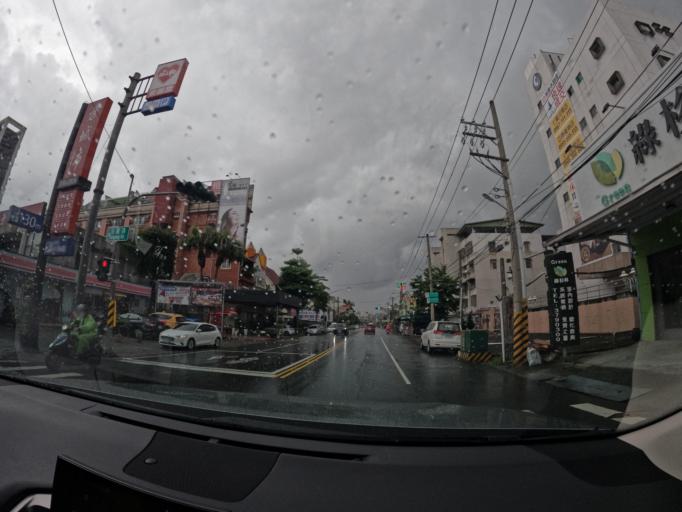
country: TW
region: Taiwan
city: Fengshan
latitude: 22.6523
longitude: 120.3402
